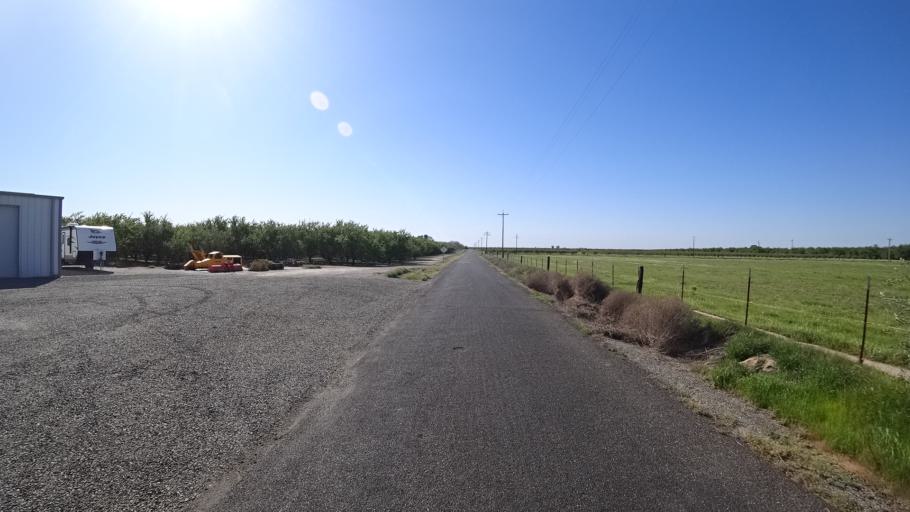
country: US
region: California
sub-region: Glenn County
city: Hamilton City
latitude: 39.7086
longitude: -122.0778
